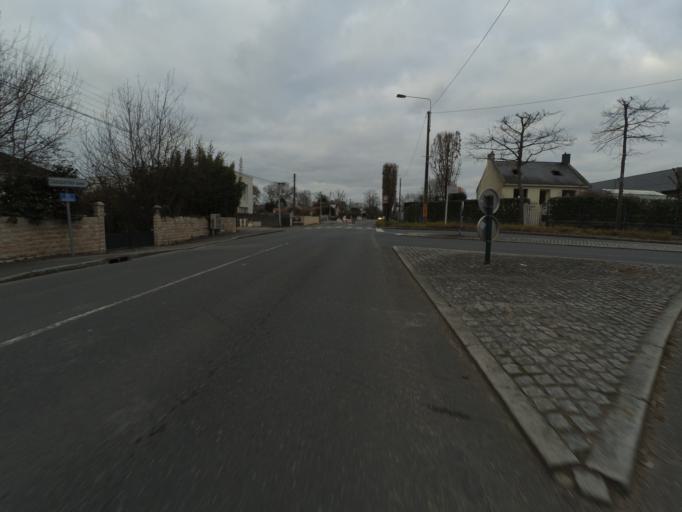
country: FR
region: Pays de la Loire
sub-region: Departement de la Loire-Atlantique
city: Carquefou
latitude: 47.2759
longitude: -1.4969
